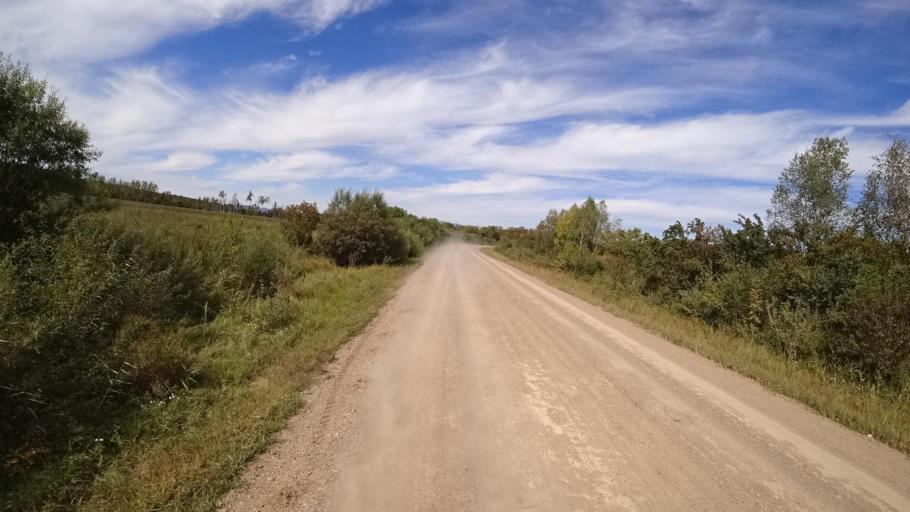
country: RU
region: Primorskiy
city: Yakovlevka
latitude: 44.6171
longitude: 133.5974
